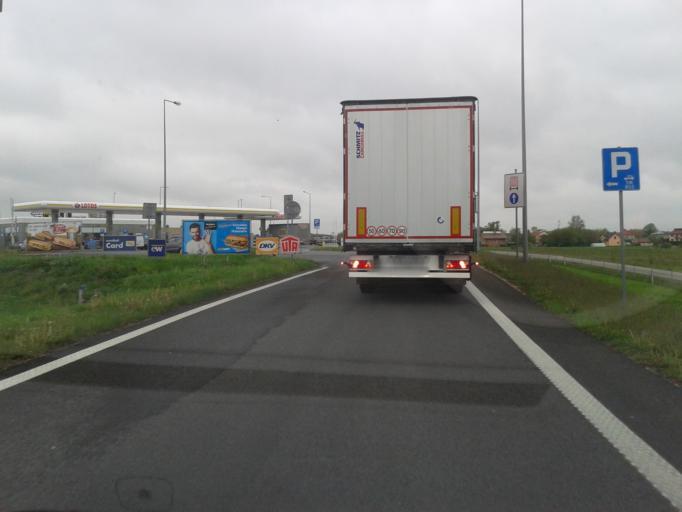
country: PL
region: Lesser Poland Voivodeship
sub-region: Powiat tarnowski
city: Wierzchoslawice
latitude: 50.0425
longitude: 20.8900
